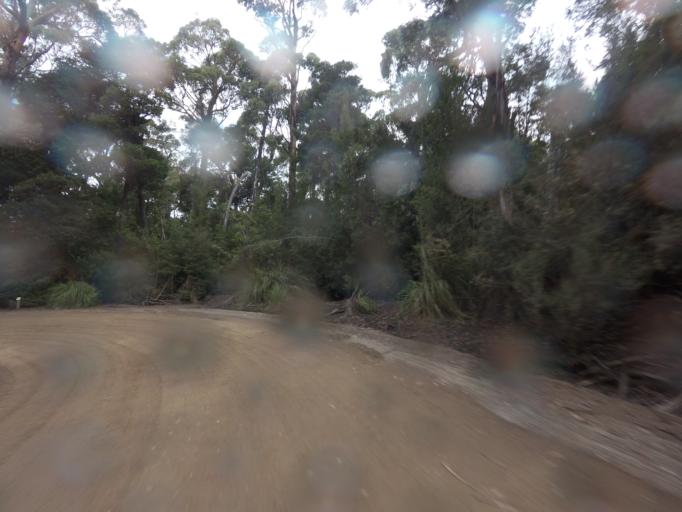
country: AU
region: Tasmania
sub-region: Derwent Valley
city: New Norfolk
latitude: -42.6822
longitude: 146.6747
